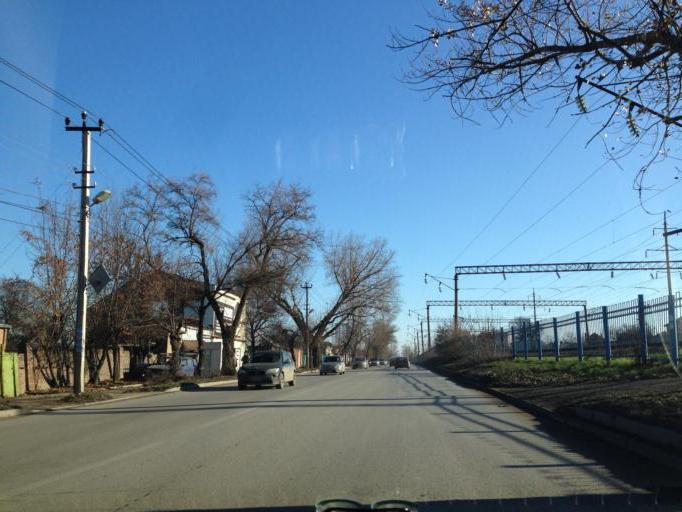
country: RU
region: Rostov
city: Rostov-na-Donu
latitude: 47.2461
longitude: 39.6793
